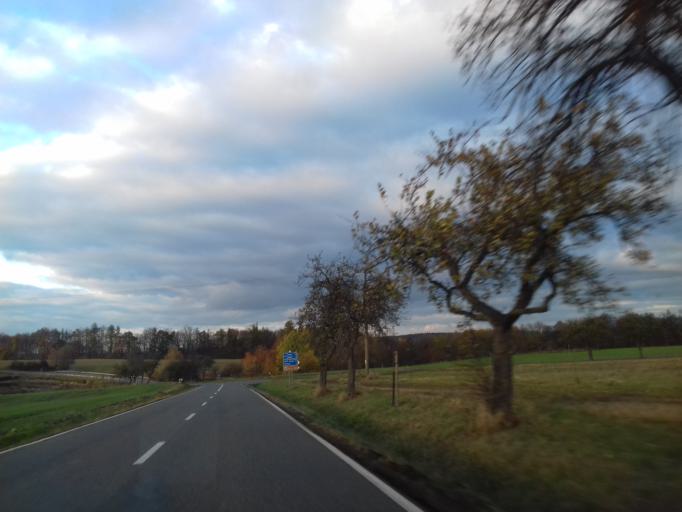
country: CZ
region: Pardubicky
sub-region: Okres Chrudim
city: Skutec
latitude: 49.8248
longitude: 16.0424
